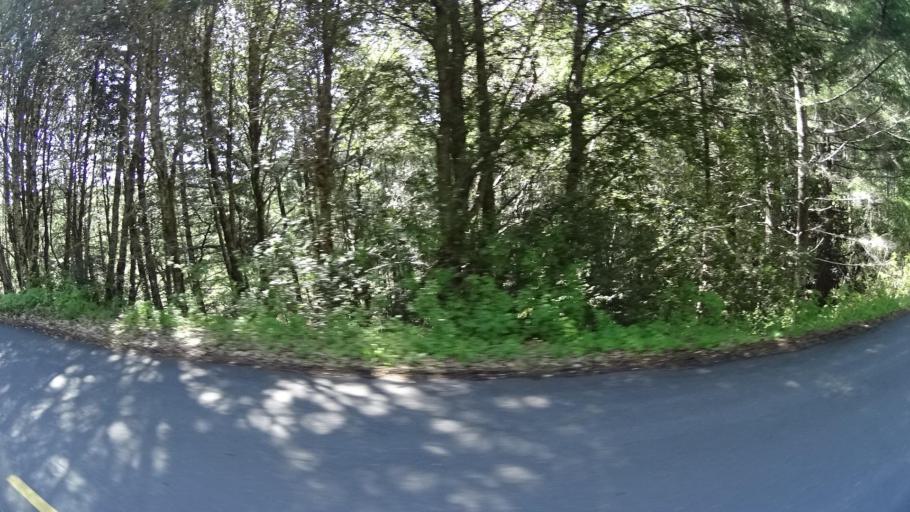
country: US
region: California
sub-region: Humboldt County
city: Rio Dell
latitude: 40.2979
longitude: -124.2506
